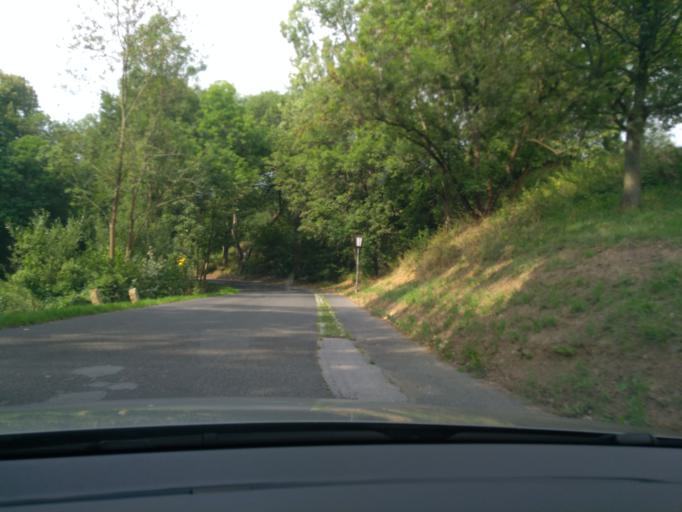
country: DE
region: Saxony
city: Markersdorf
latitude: 51.1426
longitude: 14.8772
